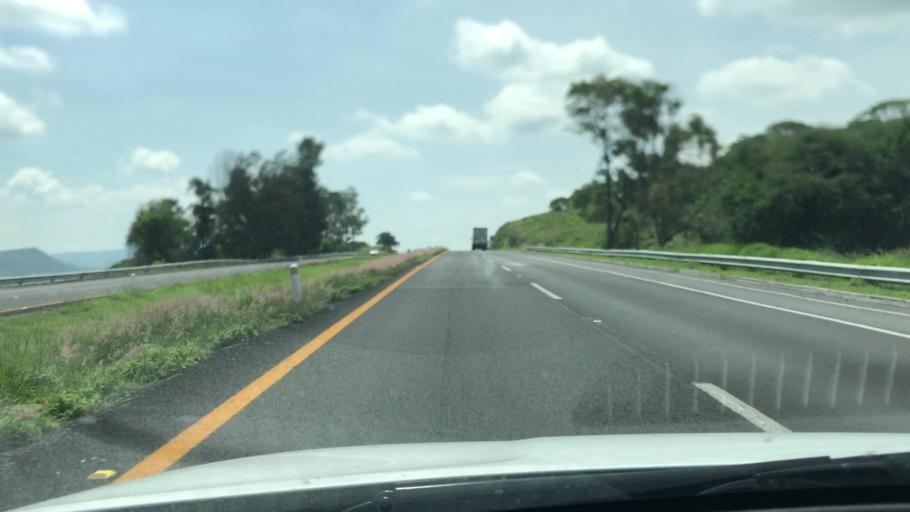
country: MX
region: Jalisco
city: Ocotlan
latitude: 20.4309
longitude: -102.7846
